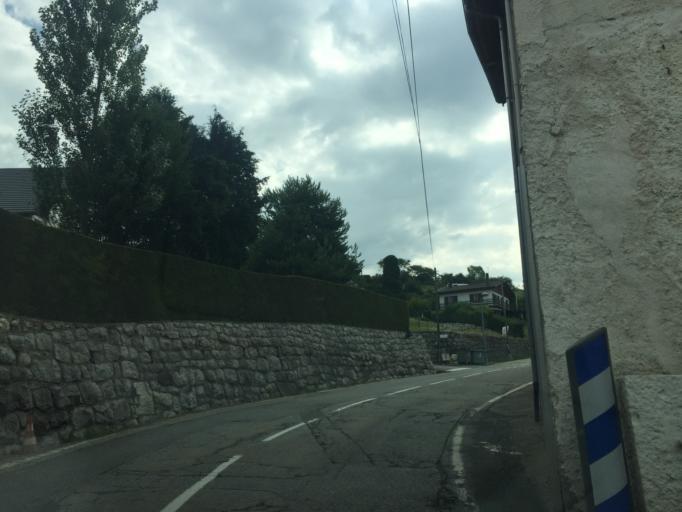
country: FR
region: Rhone-Alpes
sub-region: Departement de la Savoie
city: Barby
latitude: 45.5773
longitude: 5.9792
